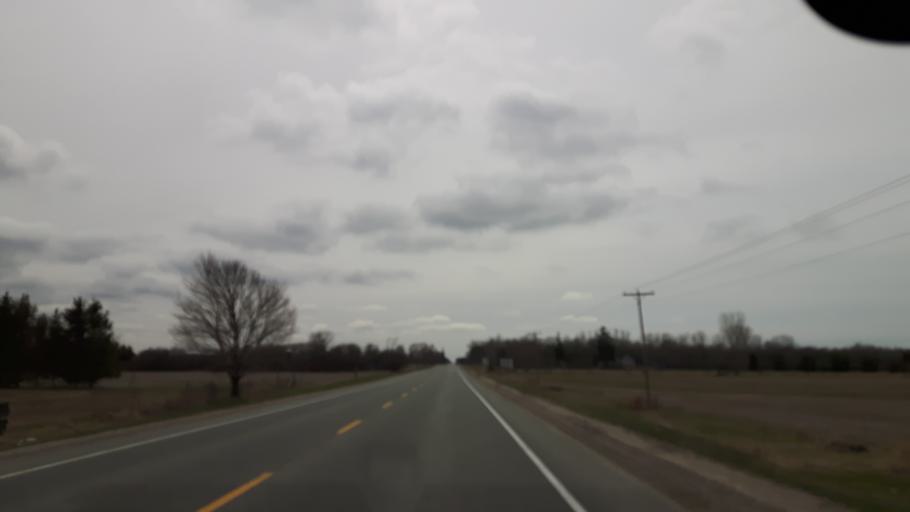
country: CA
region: Ontario
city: Goderich
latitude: 43.7066
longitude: -81.7057
